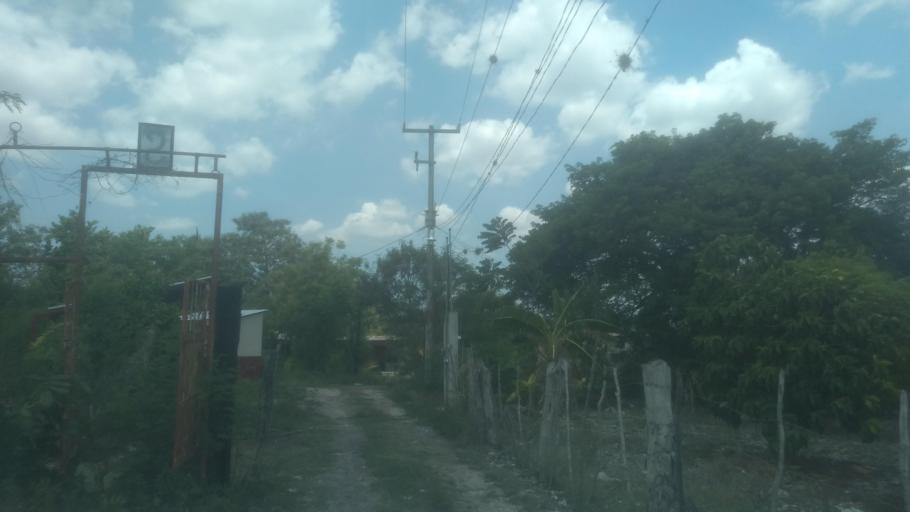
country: MX
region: Veracruz
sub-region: Emiliano Zapata
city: Plan del Rio
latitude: 19.3932
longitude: -96.6375
